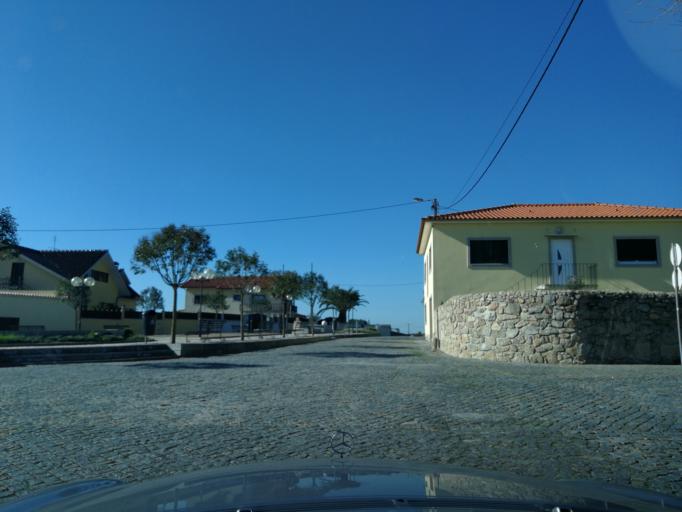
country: PT
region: Porto
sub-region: Vila do Conde
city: Vila do Conde
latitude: 41.3756
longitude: -8.7322
